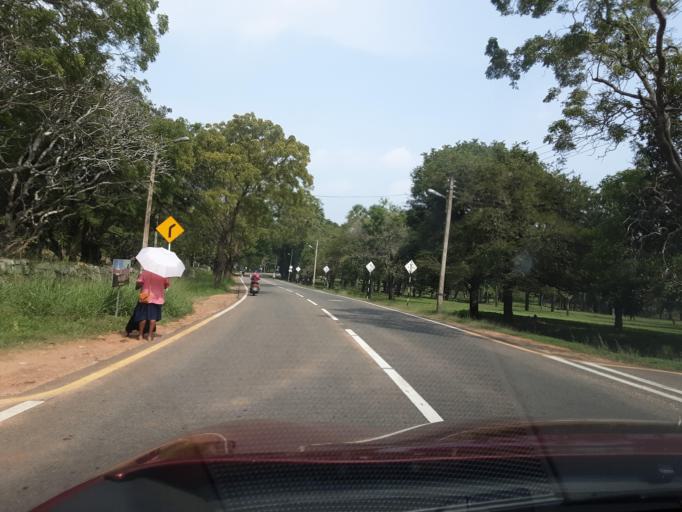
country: LK
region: North Central
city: Anuradhapura
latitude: 8.3524
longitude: 80.5096
